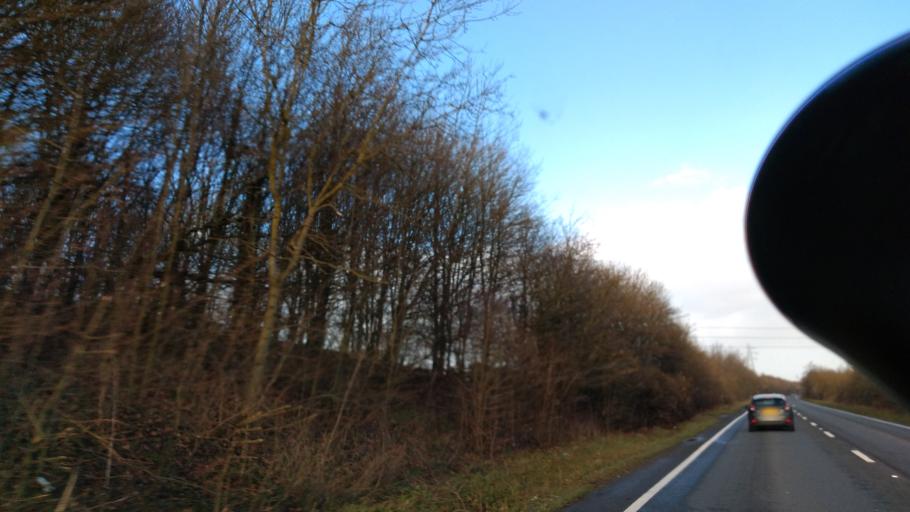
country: GB
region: England
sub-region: Somerset
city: Frome
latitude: 51.2316
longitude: -2.2973
